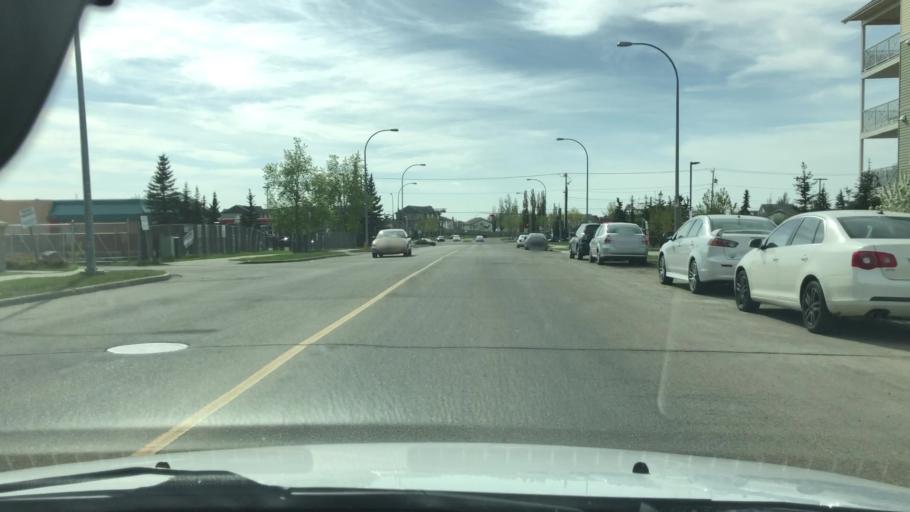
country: CA
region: Alberta
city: Edmonton
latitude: 53.6042
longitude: -113.5388
